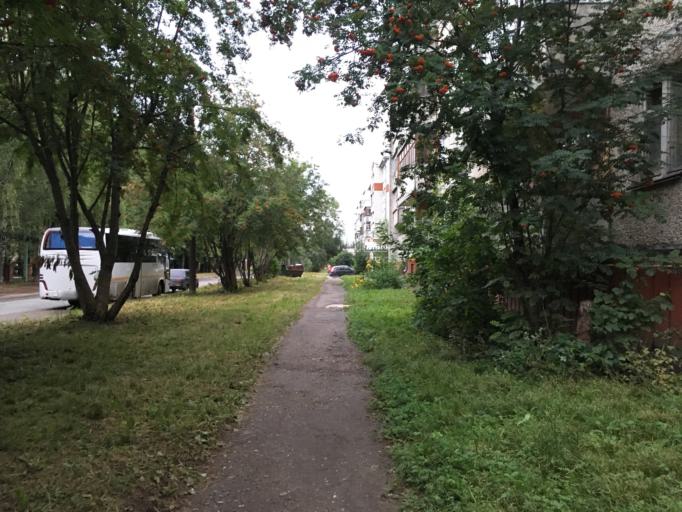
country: RU
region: Mariy-El
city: Yoshkar-Ola
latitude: 56.6485
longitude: 47.8875
